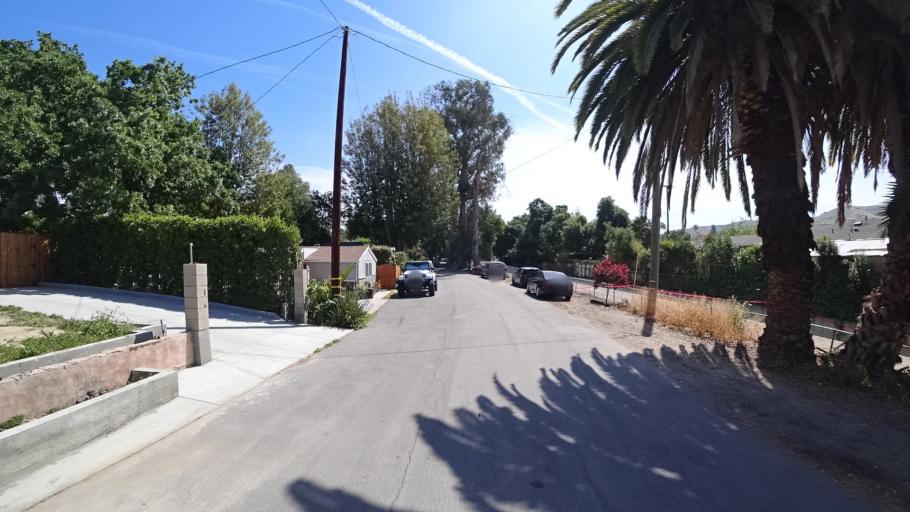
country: US
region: California
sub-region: Ventura County
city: Thousand Oaks
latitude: 34.1806
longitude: -118.8650
